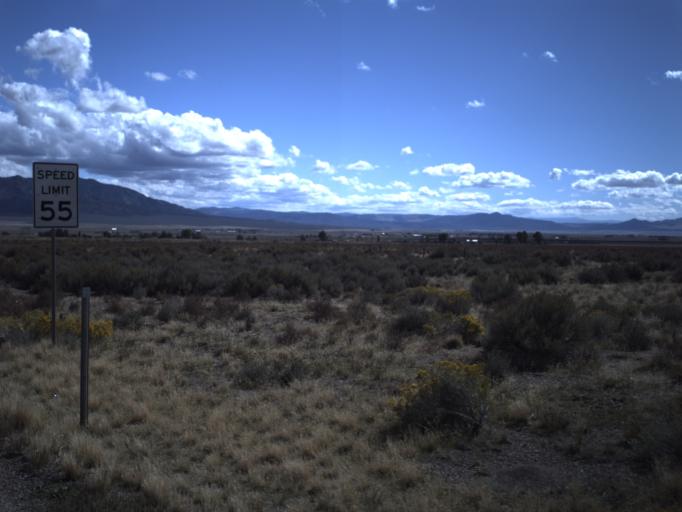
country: US
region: Utah
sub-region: Beaver County
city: Milford
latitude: 38.3996
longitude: -113.0323
